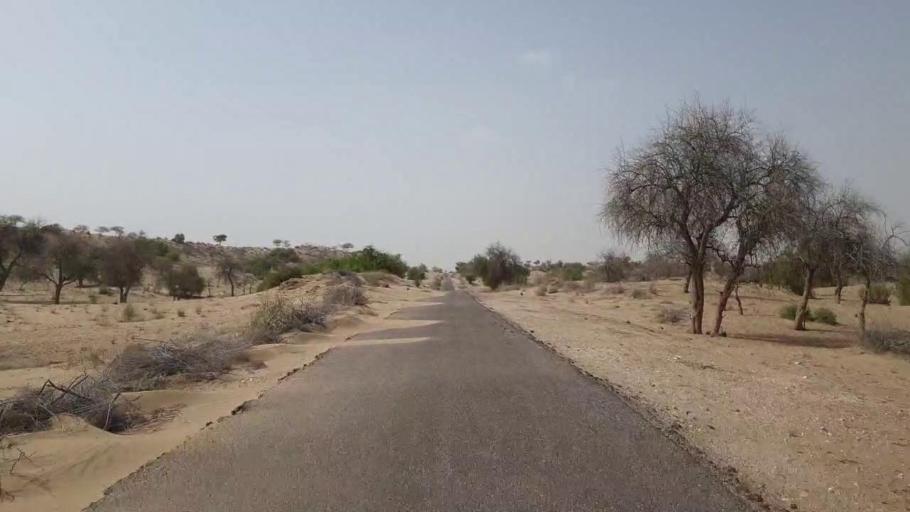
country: PK
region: Sindh
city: Mithi
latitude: 24.5841
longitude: 69.9228
